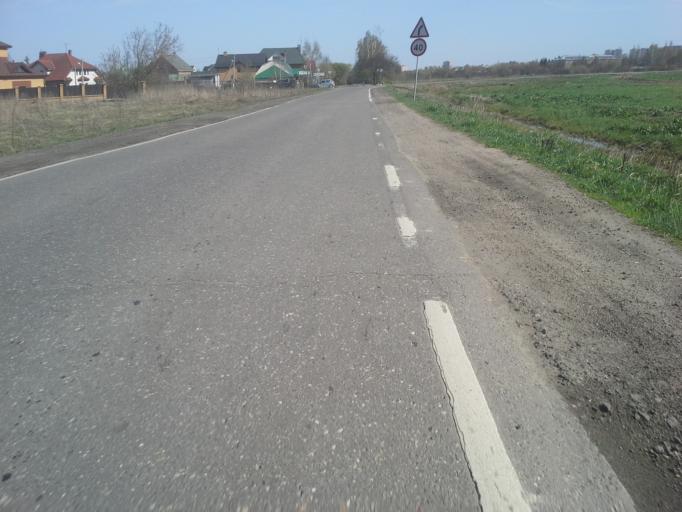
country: RU
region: Moskovskaya
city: Dubrovitsy
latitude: 55.4484
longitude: 37.4768
